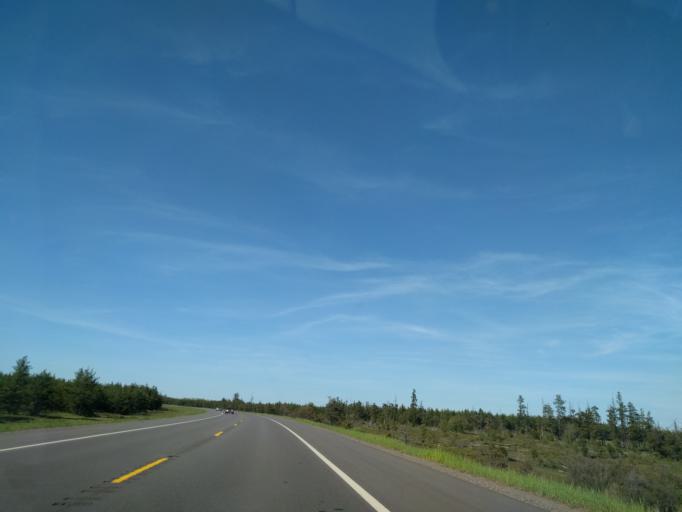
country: US
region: Michigan
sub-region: Marquette County
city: K. I. Sawyer Air Force Base
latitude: 46.3530
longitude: -87.4098
